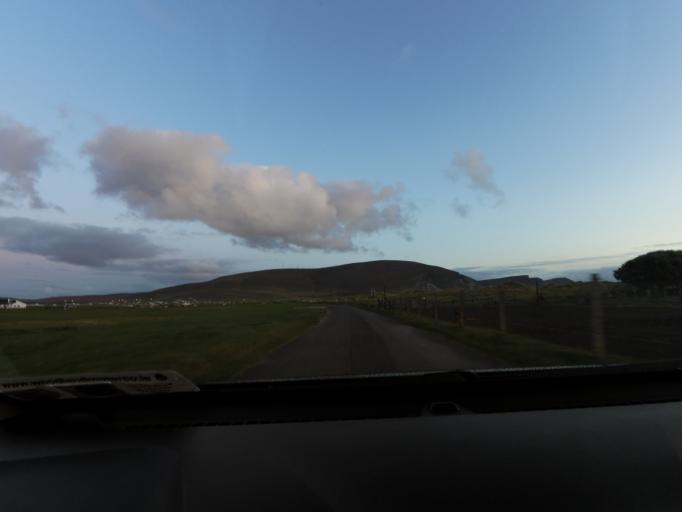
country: IE
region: Connaught
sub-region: Maigh Eo
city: Belmullet
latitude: 53.9745
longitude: -10.0818
